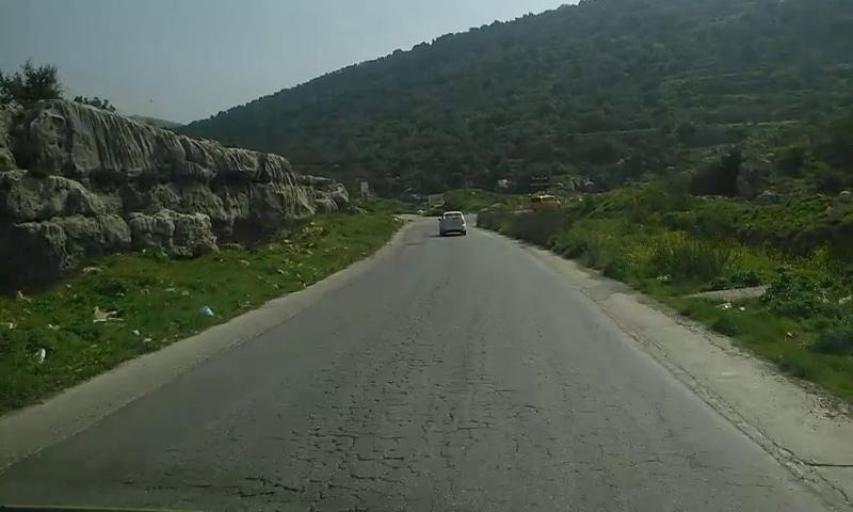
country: PS
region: West Bank
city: Dura al Qar`
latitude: 31.9559
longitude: 35.2366
